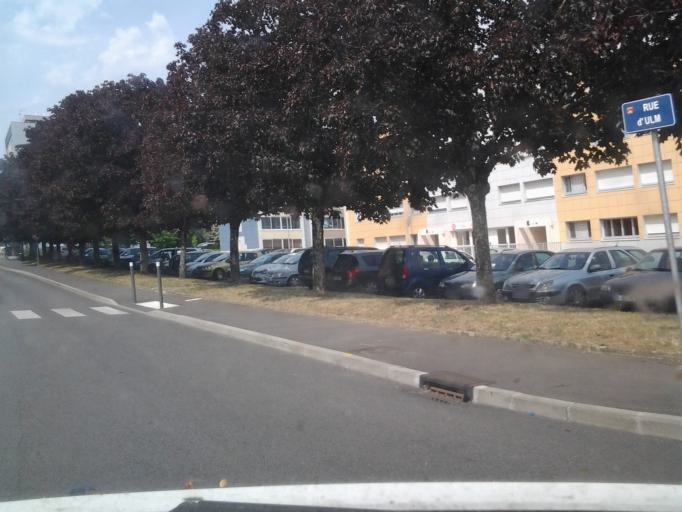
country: FR
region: Pays de la Loire
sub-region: Departement de la Vendee
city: La Roche-sur-Yon
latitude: 46.6805
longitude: -1.4284
